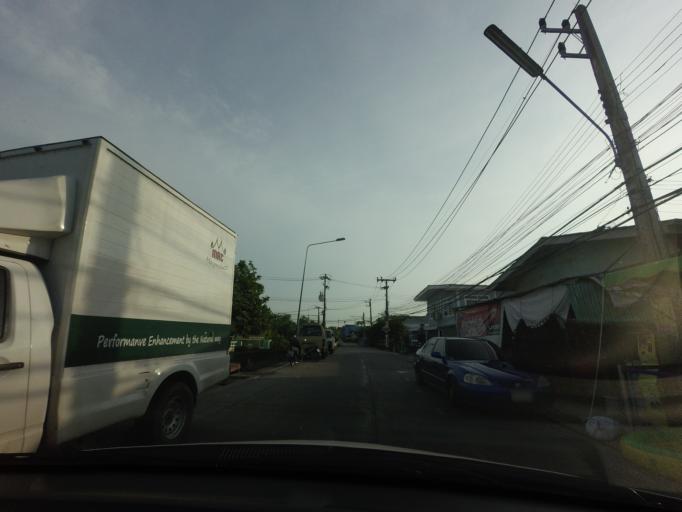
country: TH
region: Pathum Thani
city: Pathum Thani
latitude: 14.0366
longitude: 100.5446
